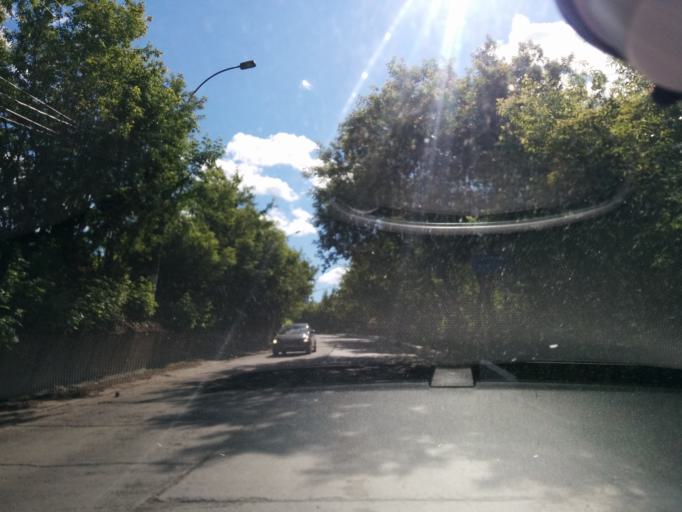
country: RU
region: Perm
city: Perm
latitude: 58.0136
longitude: 56.2060
